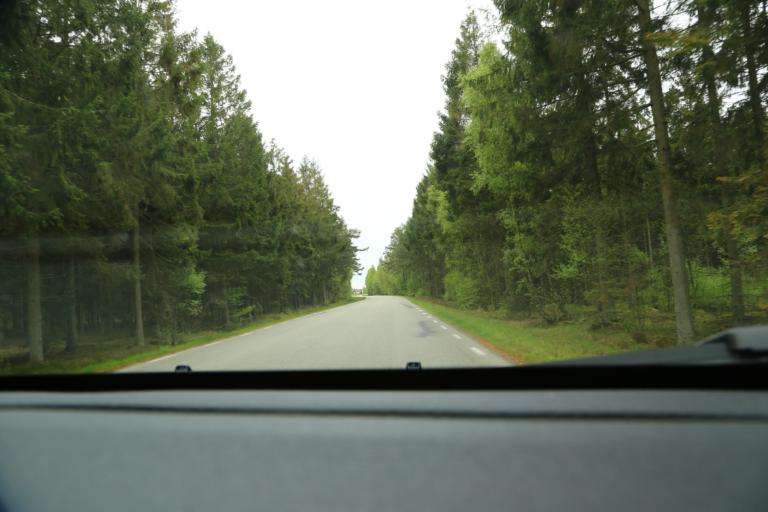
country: SE
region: Halland
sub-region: Varbergs Kommun
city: Tvaaker
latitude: 57.0476
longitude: 12.3618
